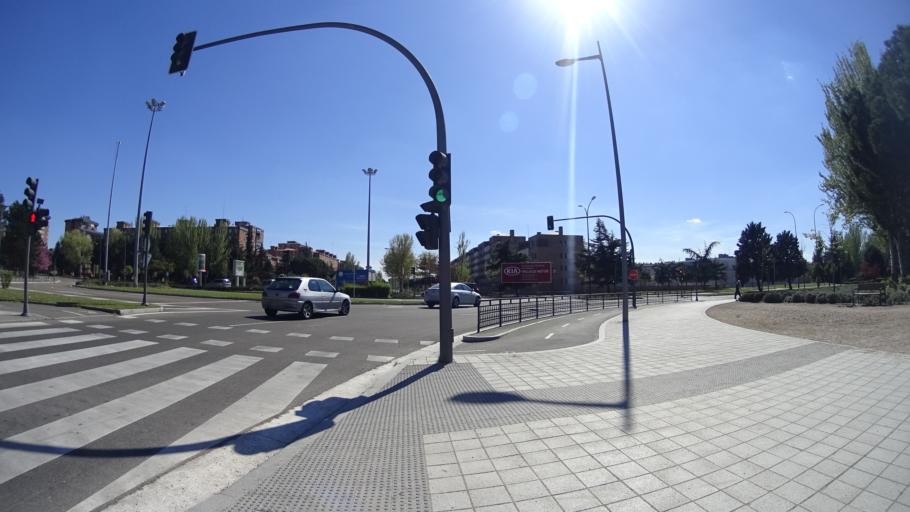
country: ES
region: Castille and Leon
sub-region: Provincia de Valladolid
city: Valladolid
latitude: 41.6485
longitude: -4.7408
